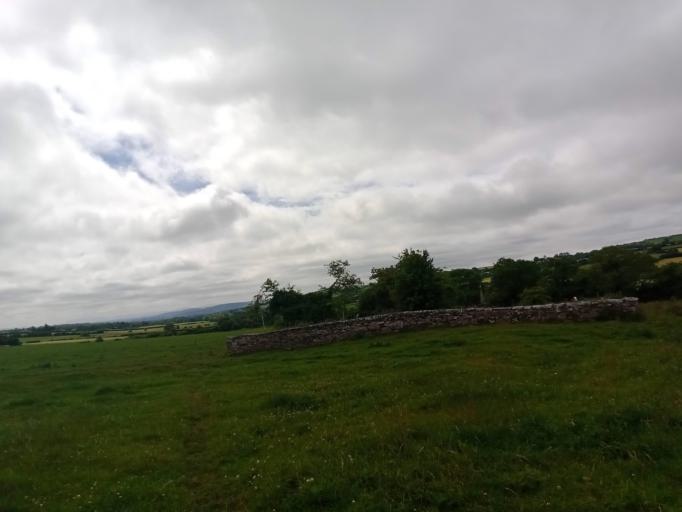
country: IE
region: Leinster
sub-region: Kilkenny
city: Ballyragget
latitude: 52.7716
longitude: -7.4659
